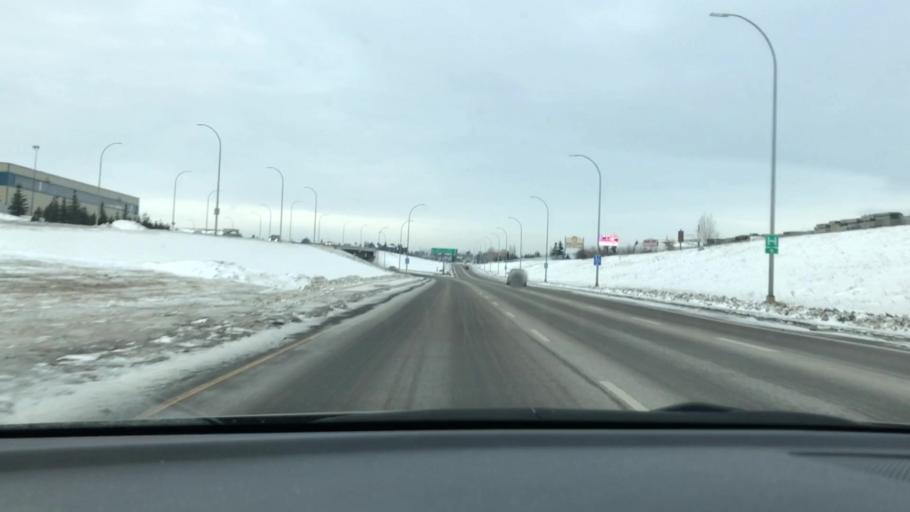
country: CA
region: Alberta
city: Edmonton
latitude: 53.5153
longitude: -113.4265
